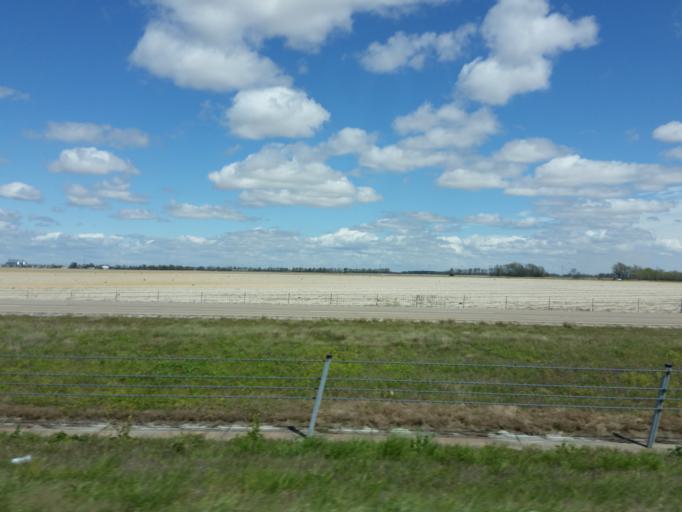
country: US
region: Arkansas
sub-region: Craighead County
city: Bay
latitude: 35.7776
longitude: -90.5898
